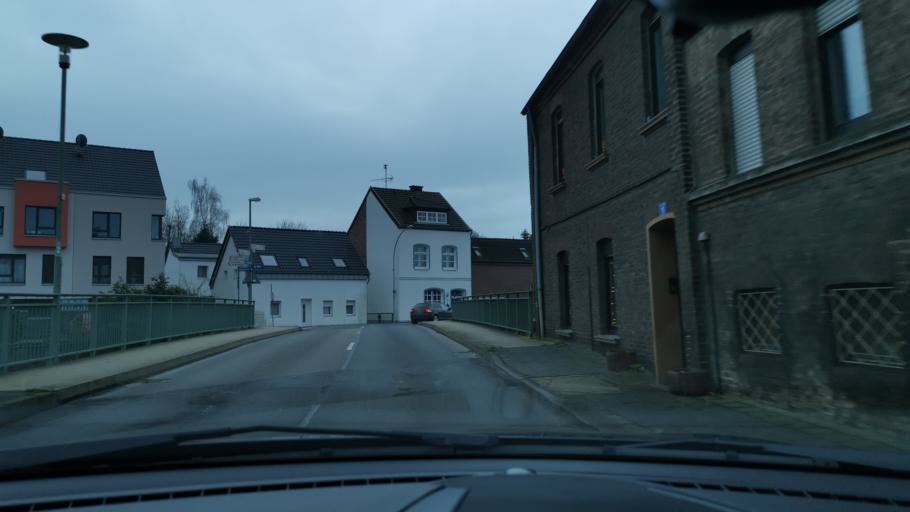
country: DE
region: North Rhine-Westphalia
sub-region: Regierungsbezirk Dusseldorf
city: Neubrueck
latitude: 51.1124
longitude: 6.6263
